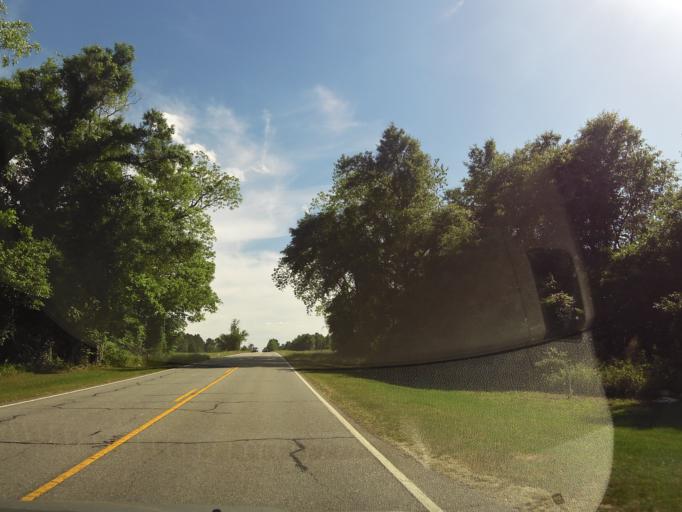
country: US
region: South Carolina
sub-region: Bamberg County
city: Denmark
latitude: 33.1933
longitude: -81.1806
